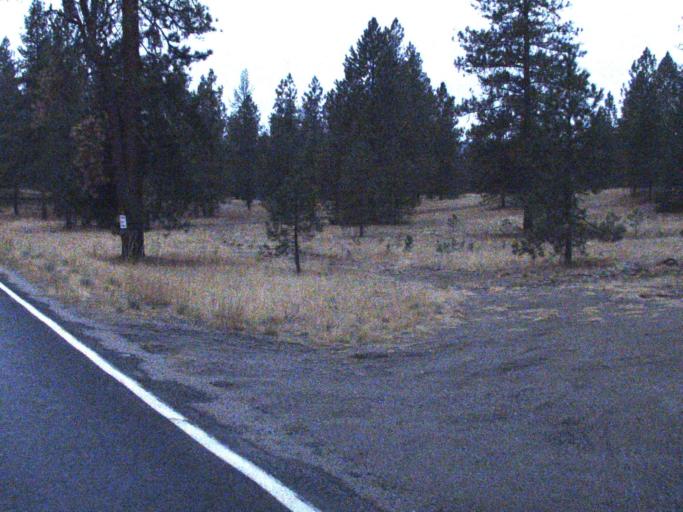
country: US
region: Washington
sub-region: Spokane County
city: Fairchild Air Force Base
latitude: 47.8893
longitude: -117.8313
